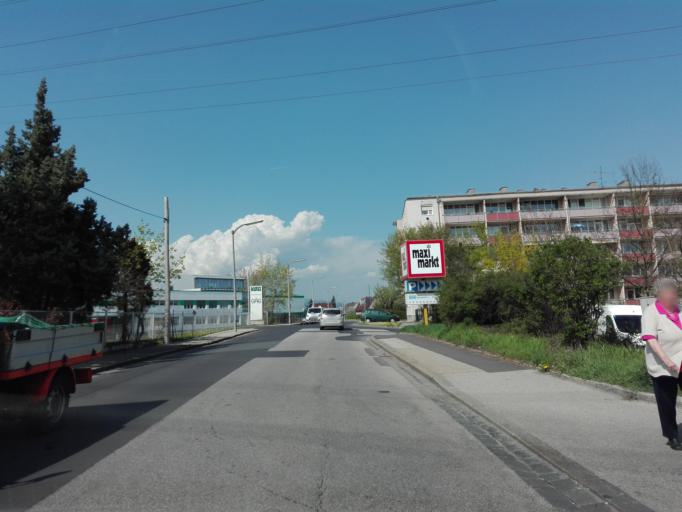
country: AT
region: Upper Austria
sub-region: Politischer Bezirk Linz-Land
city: Ansfelden
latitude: 48.2443
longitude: 14.2762
